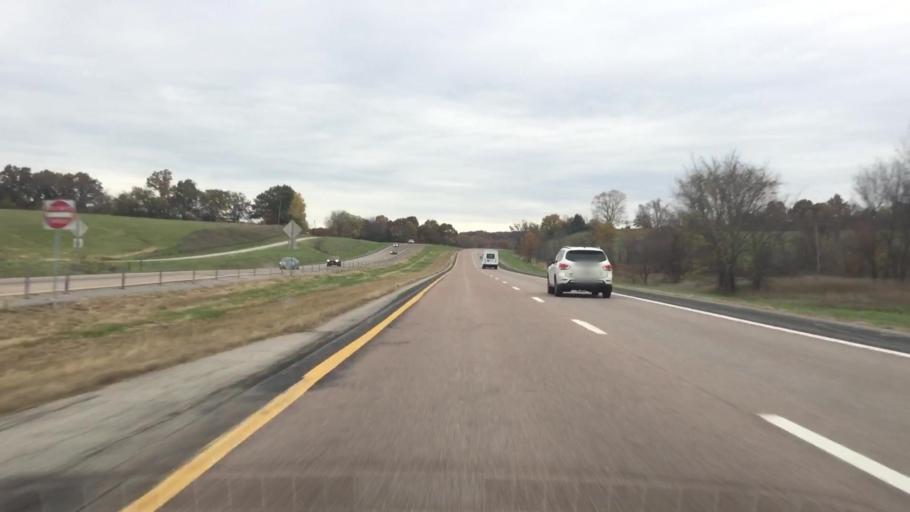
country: US
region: Missouri
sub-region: Cole County
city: Jefferson City
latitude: 38.6514
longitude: -92.2068
